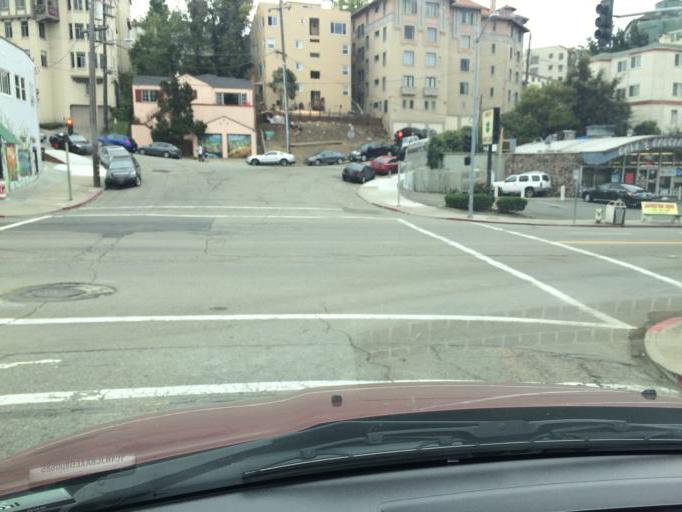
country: US
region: California
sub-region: Alameda County
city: Piedmont
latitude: 37.8026
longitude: -122.2416
